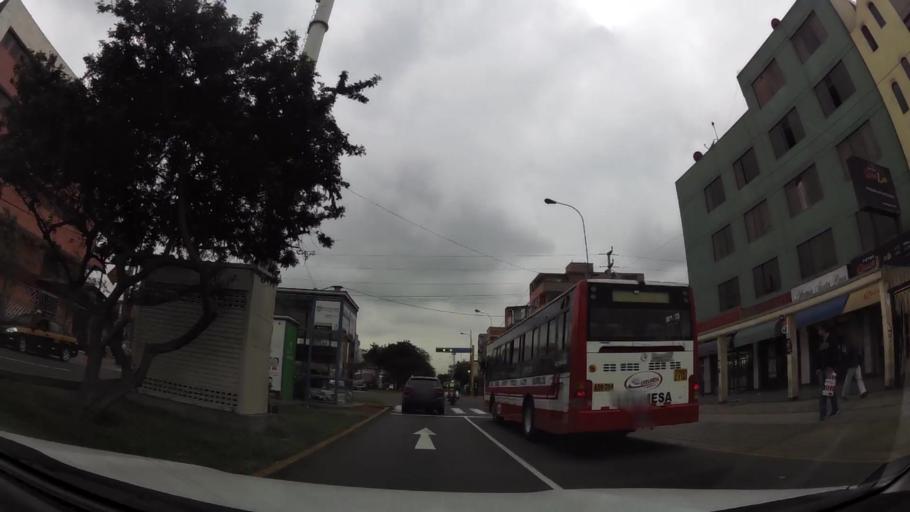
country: PE
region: Lima
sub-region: Lima
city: Surco
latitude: -12.1437
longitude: -76.9852
